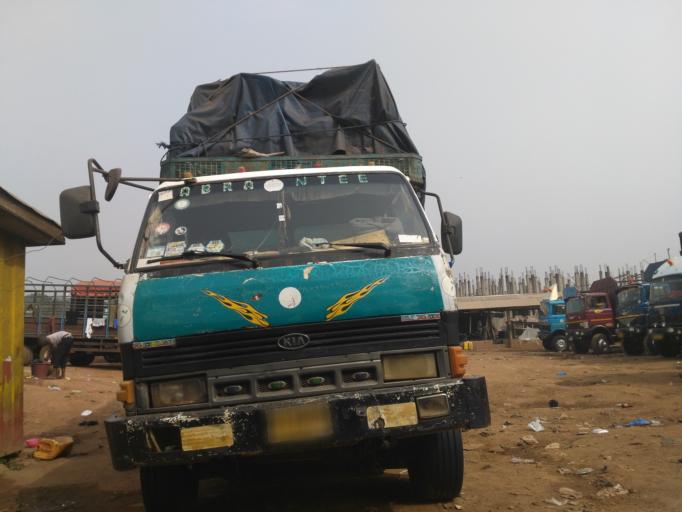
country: GH
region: Ashanti
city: Kumasi
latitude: 6.6952
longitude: -1.6078
